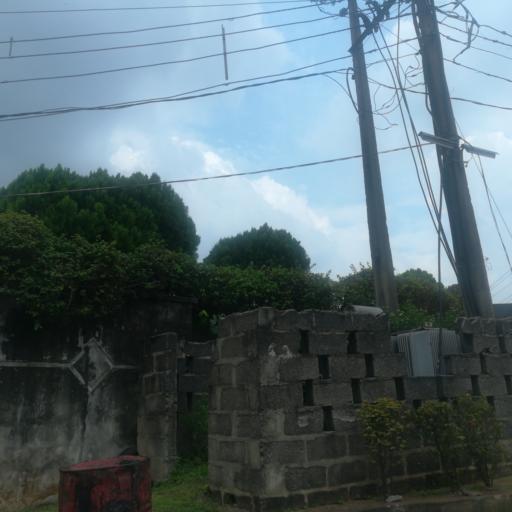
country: NG
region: Lagos
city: Ojota
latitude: 6.5736
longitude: 3.3918
